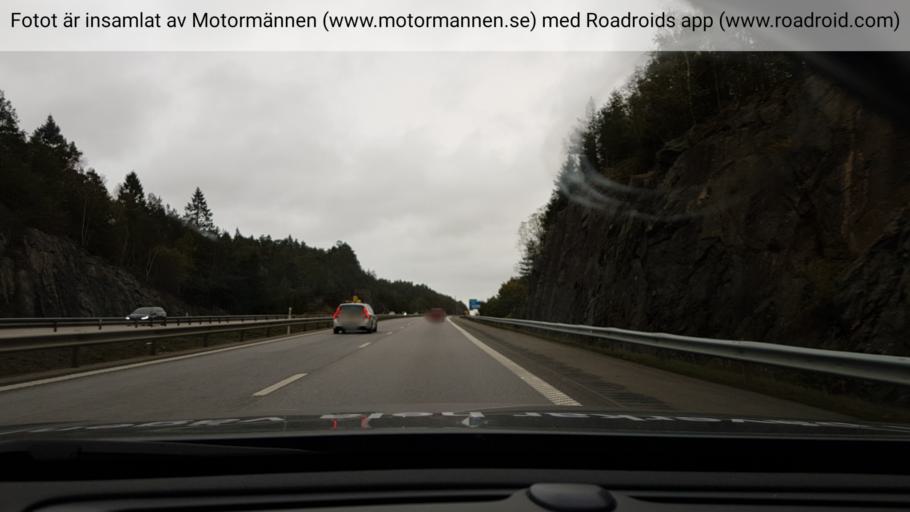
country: SE
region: Vaestra Goetaland
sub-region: Harryda Kommun
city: Molnlycke
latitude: 57.6750
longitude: 12.1356
